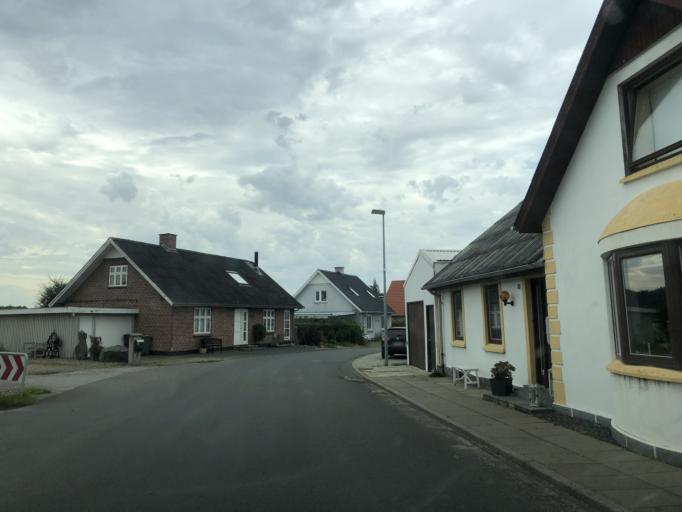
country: DK
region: Central Jutland
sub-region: Holstebro Kommune
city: Holstebro
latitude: 56.3770
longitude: 8.5223
